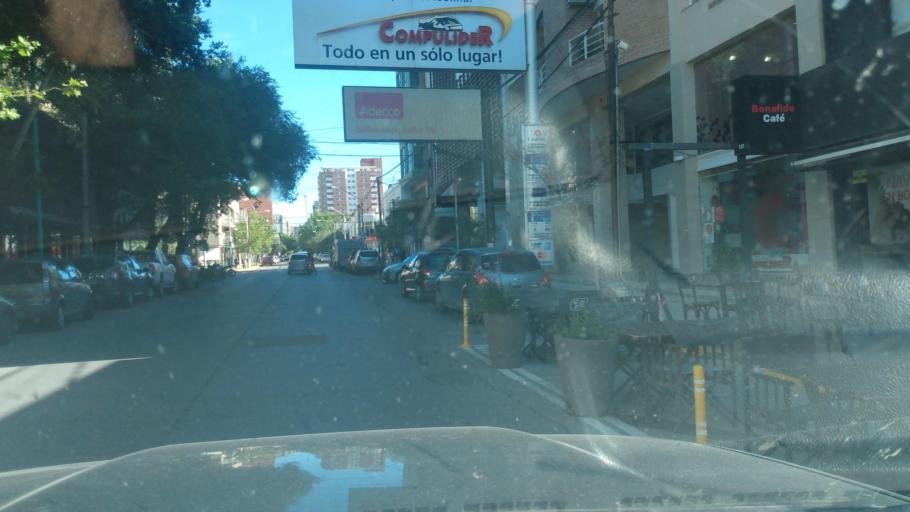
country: AR
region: Neuquen
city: Neuquen
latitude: -38.9537
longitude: -68.0608
